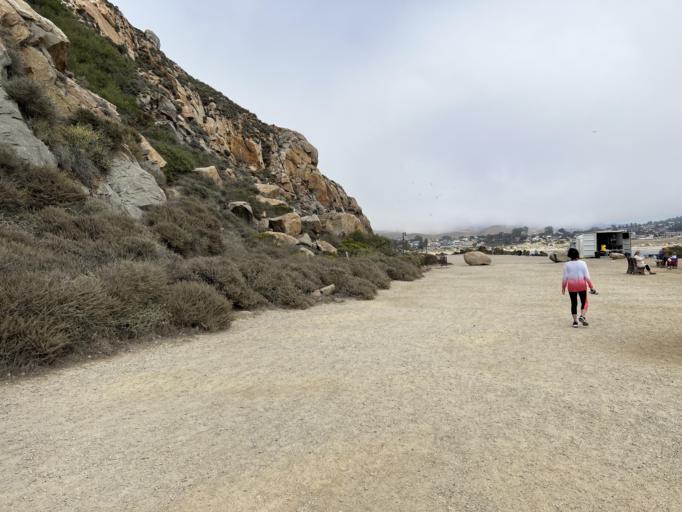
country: US
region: California
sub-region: San Luis Obispo County
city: Morro Bay
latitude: 35.3677
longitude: -120.8683
